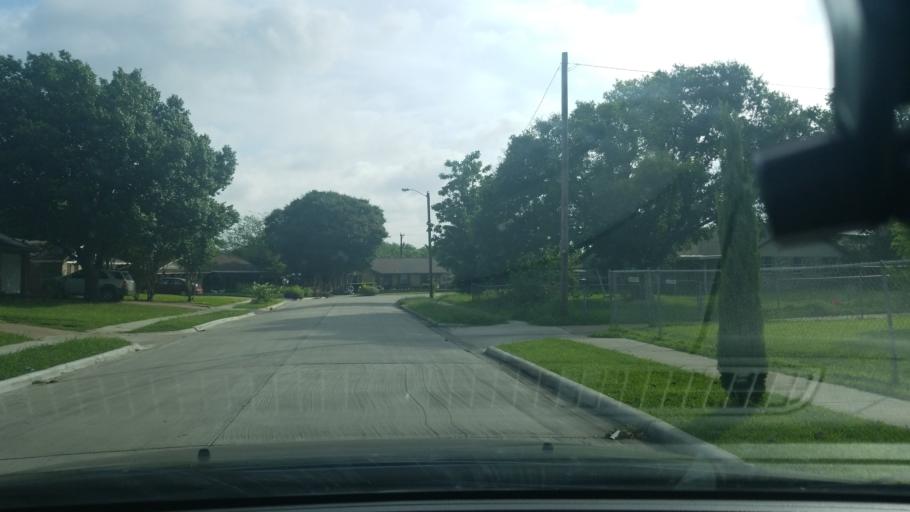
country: US
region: Texas
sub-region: Dallas County
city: Mesquite
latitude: 32.7740
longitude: -96.6431
